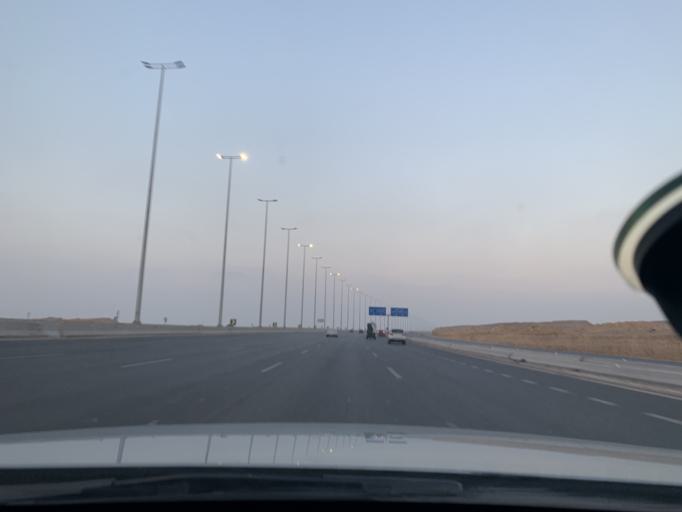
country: EG
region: Muhafazat al Qalyubiyah
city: Al Khankah
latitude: 30.0946
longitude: 31.4861
